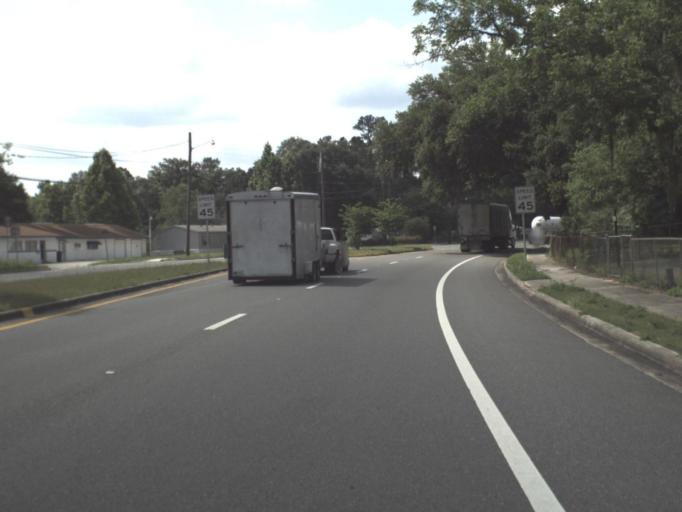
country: US
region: Florida
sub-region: Alachua County
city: Waldo
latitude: 29.7811
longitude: -82.1671
